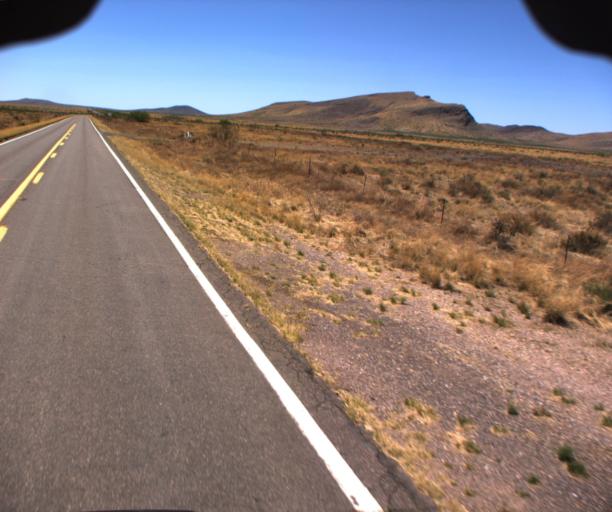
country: US
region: Arizona
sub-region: Cochise County
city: Douglas
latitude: 31.6904
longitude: -109.1326
